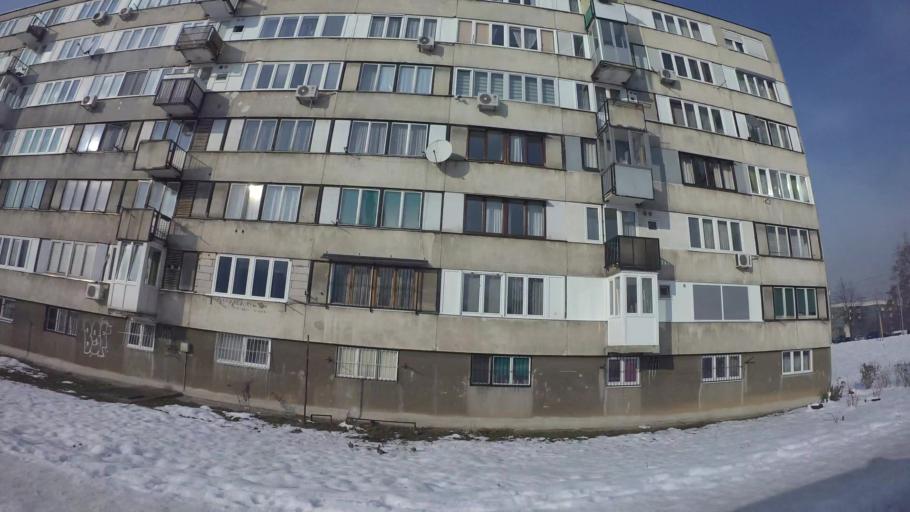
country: BA
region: Federation of Bosnia and Herzegovina
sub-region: Kanton Sarajevo
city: Sarajevo
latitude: 43.8471
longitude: 18.3731
